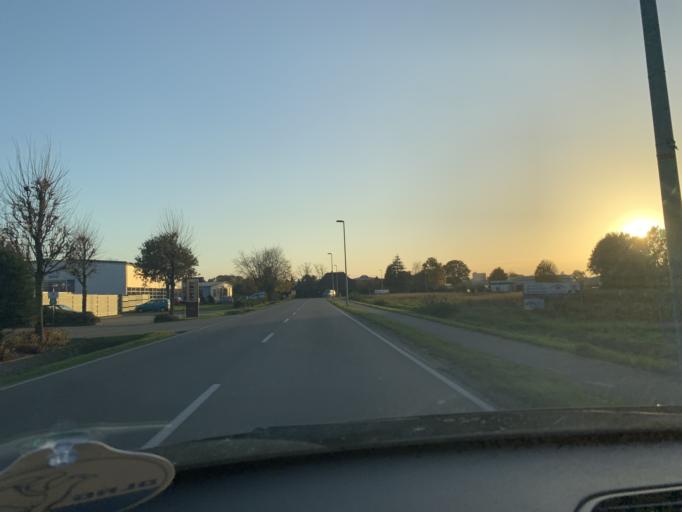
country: DE
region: Lower Saxony
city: Edewecht
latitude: 53.1232
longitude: 8.0031
